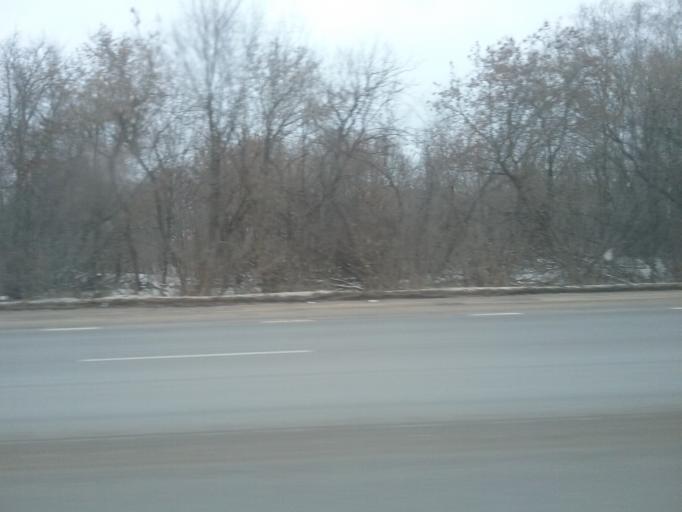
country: RU
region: Tula
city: Tula
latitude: 54.1451
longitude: 37.6514
